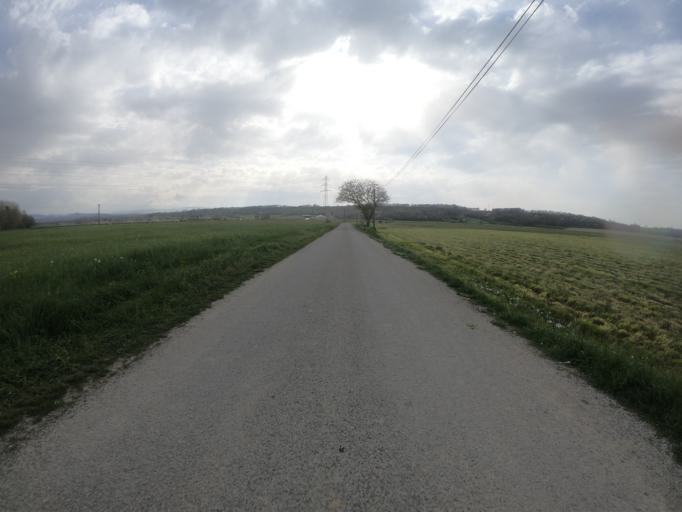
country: FR
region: Languedoc-Roussillon
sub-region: Departement de l'Aude
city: Belpech
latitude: 43.1237
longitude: 1.7323
